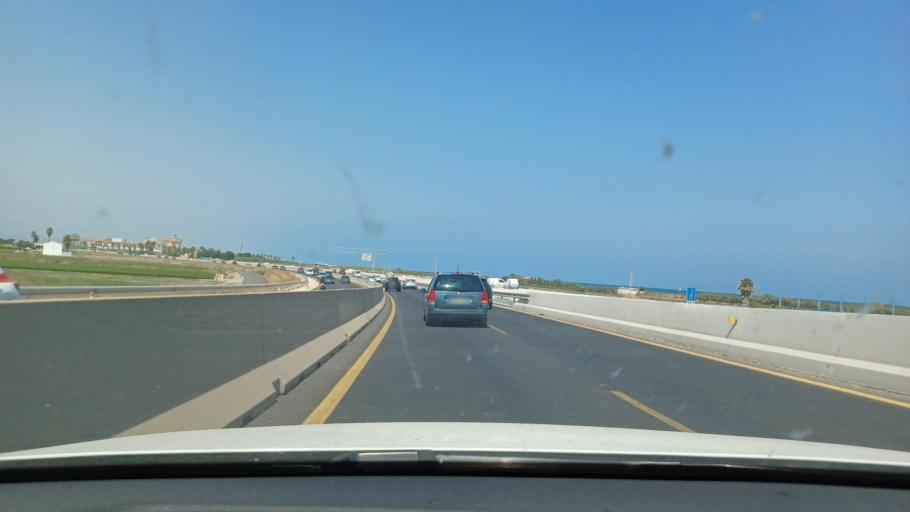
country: ES
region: Valencia
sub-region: Provincia de Valencia
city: Alboraya
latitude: 39.4951
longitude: -0.3270
